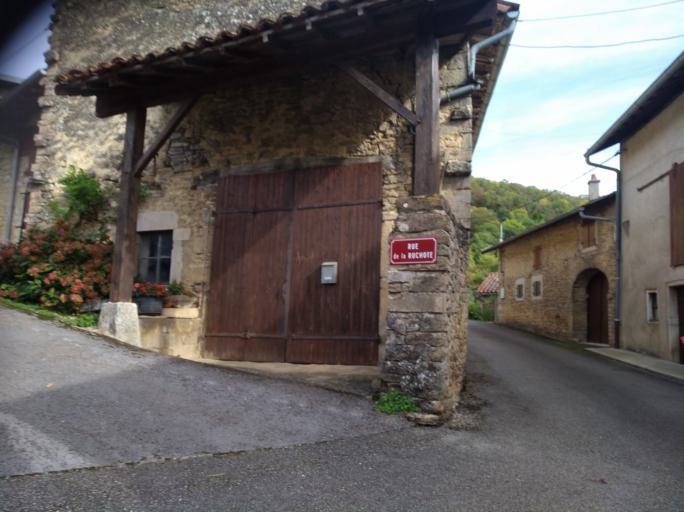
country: FR
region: Bourgogne
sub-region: Departement de Saone-et-Loire
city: Cuiseaux
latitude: 46.4593
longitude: 5.3868
